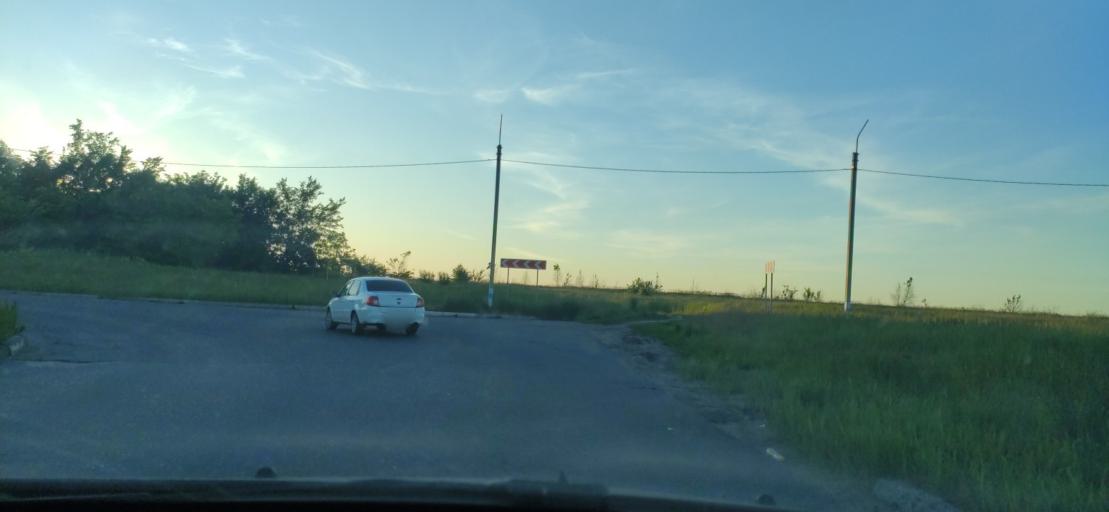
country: RU
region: Ulyanovsk
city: Mirnyy
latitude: 54.3788
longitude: 48.6717
